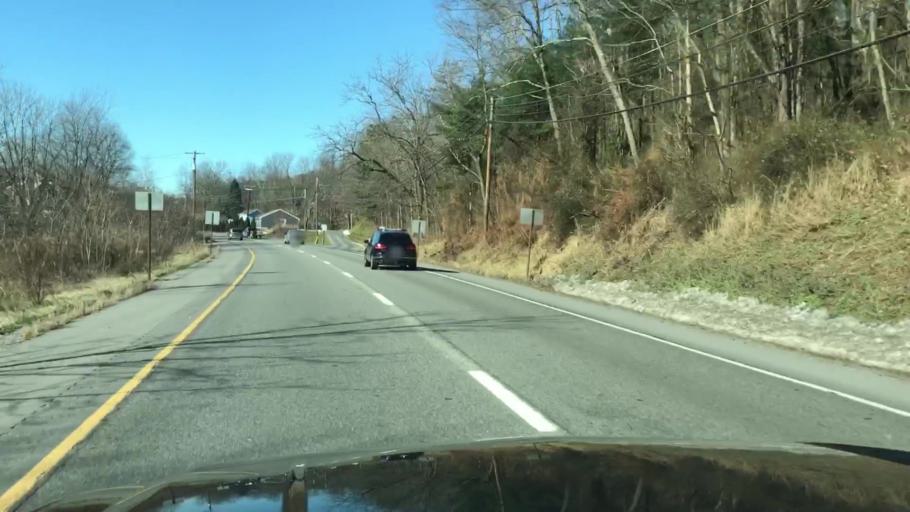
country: US
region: Pennsylvania
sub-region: Snyder County
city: Shamokin Dam
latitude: 40.8736
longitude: -76.8257
